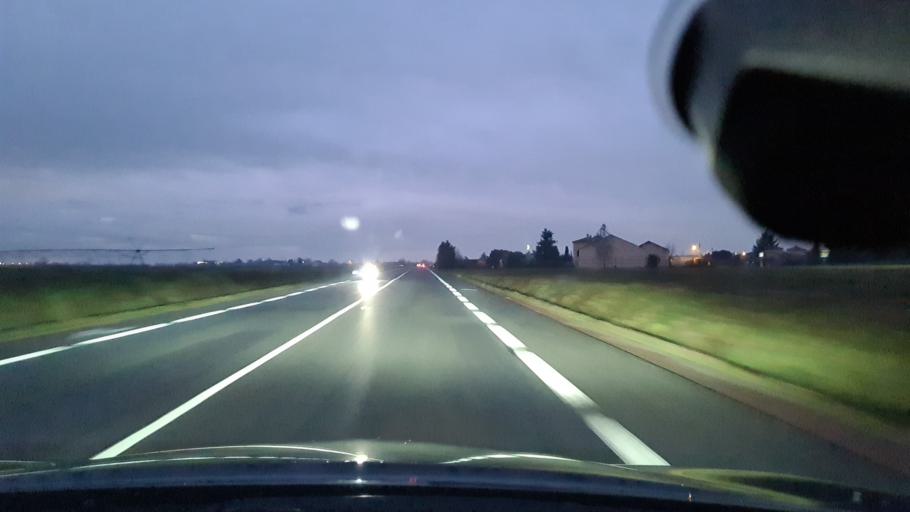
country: FR
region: Rhone-Alpes
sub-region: Departement du Rhone
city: Meyzieu
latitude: 45.7503
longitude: 5.0198
